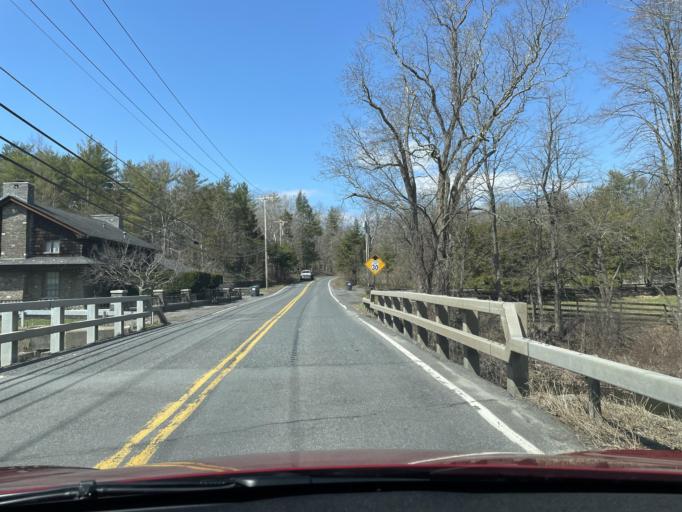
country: US
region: New York
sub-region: Ulster County
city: Manorville
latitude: 42.1043
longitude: -74.0184
